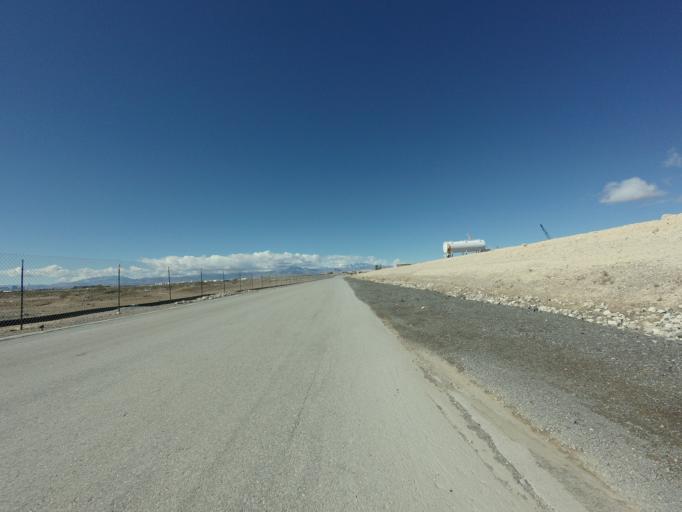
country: US
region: Nevada
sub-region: Clark County
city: Nellis Air Force Base
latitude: 36.2584
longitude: -115.0287
